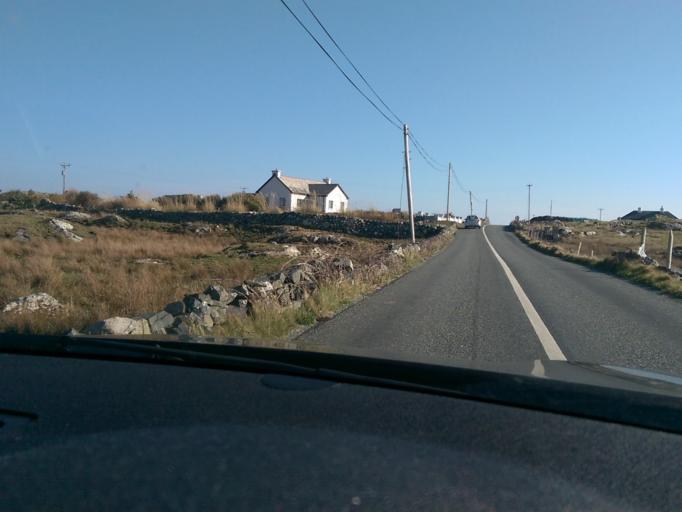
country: IE
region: Connaught
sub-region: County Galway
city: Clifden
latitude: 53.4046
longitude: -10.0324
